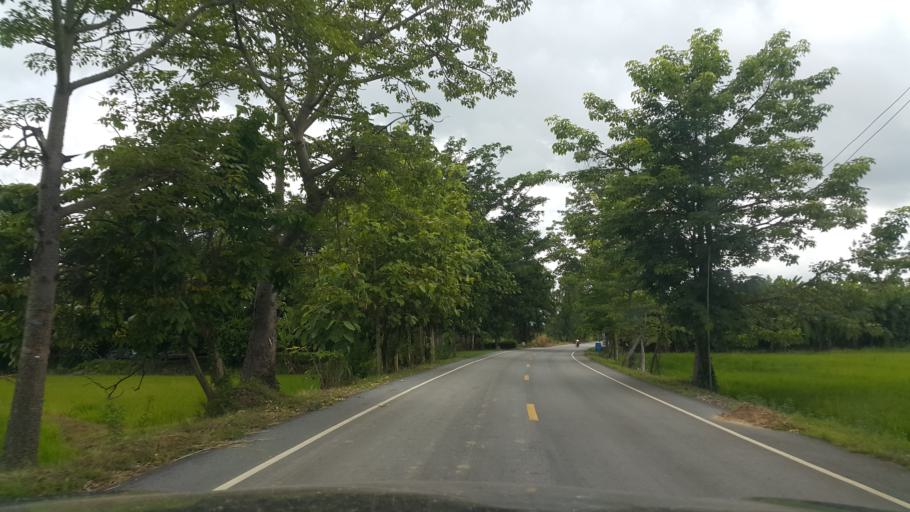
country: TH
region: Sukhothai
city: Kong Krailat
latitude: 16.9123
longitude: 99.8865
